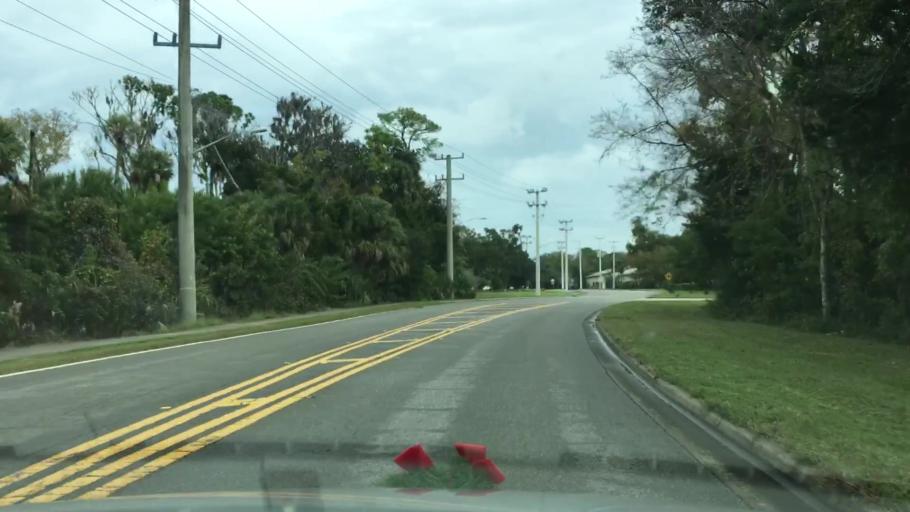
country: US
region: Florida
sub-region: Volusia County
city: Ormond Beach
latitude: 29.2880
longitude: -81.0752
